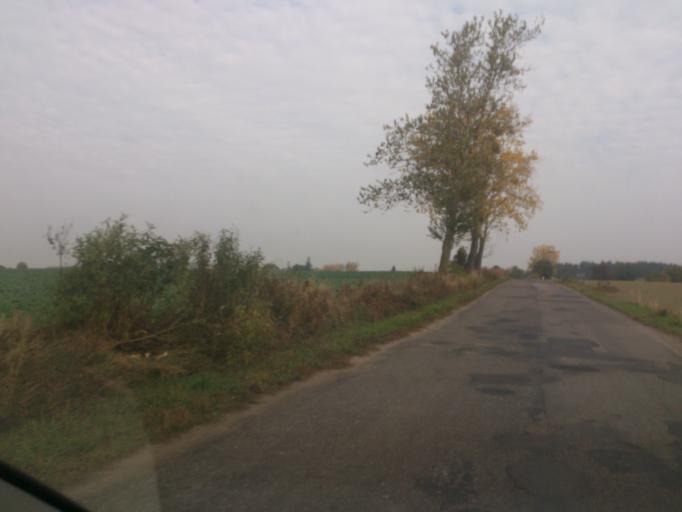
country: PL
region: Kujawsko-Pomorskie
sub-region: Powiat golubsko-dobrzynski
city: Golub-Dobrzyn
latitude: 53.1316
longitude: 19.0704
